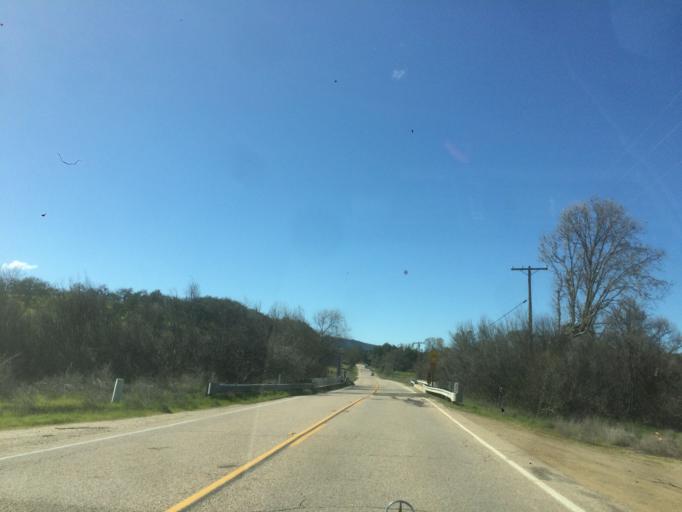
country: US
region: California
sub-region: San Luis Obispo County
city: Santa Margarita
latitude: 35.3886
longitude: -120.5811
